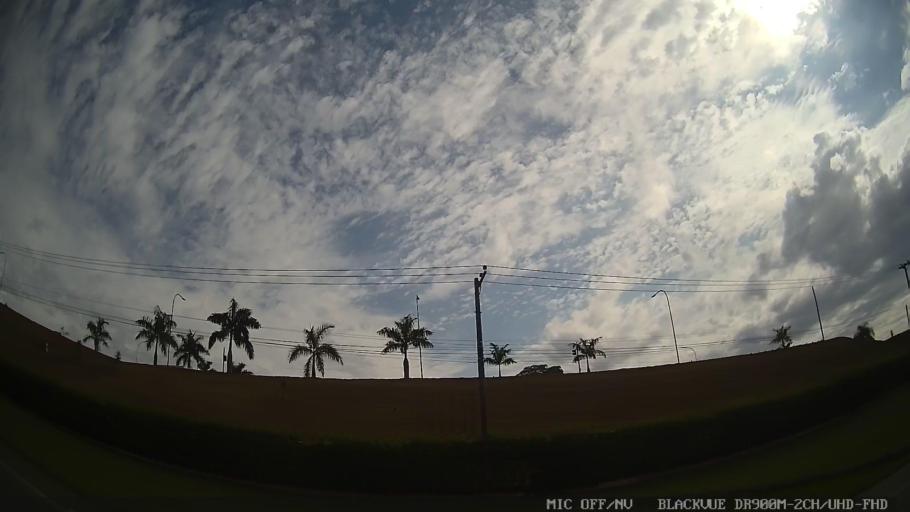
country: BR
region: Sao Paulo
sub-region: Salto
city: Salto
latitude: -23.1539
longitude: -47.2581
